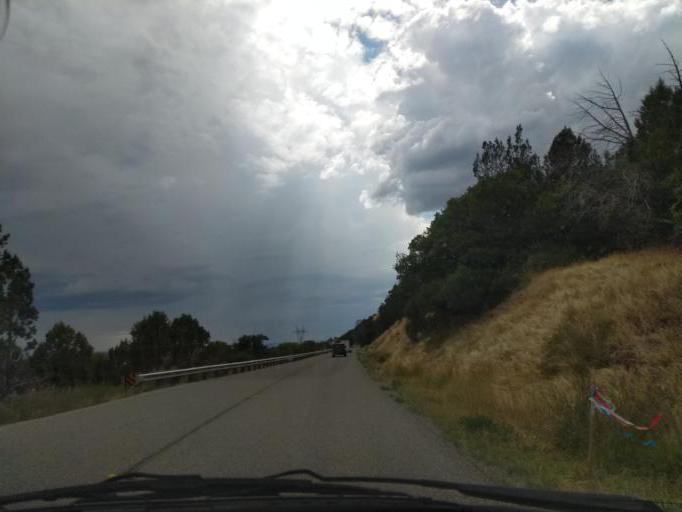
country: US
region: Colorado
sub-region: Delta County
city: Paonia
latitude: 38.8987
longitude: -107.5671
